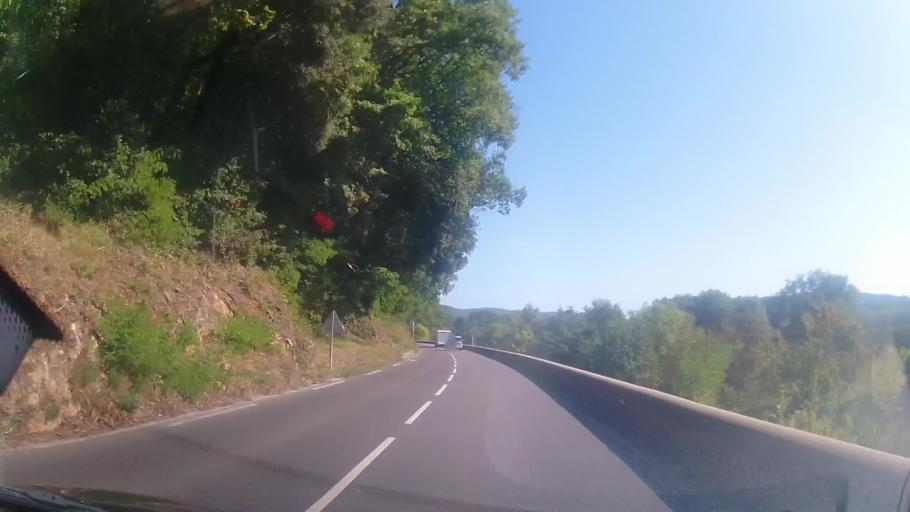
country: FR
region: Aquitaine
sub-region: Departement de la Dordogne
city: Eyvigues-et-Eybenes
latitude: 44.8644
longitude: 1.3525
